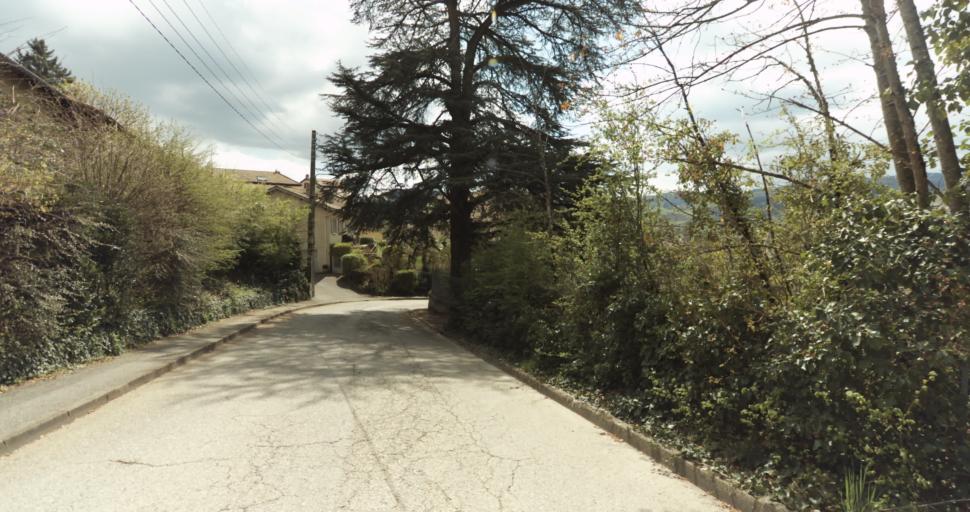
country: FR
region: Rhone-Alpes
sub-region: Departement du Rhone
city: Tarare
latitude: 45.8975
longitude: 4.4390
